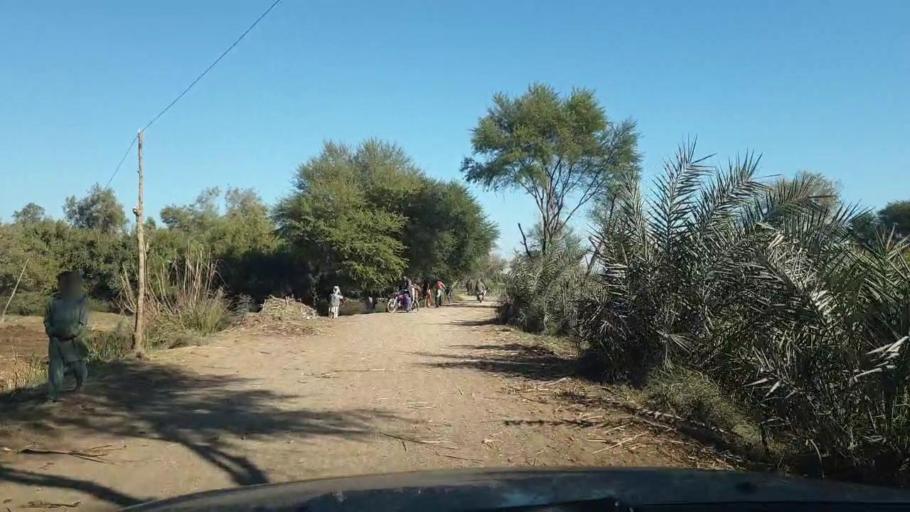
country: PK
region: Sindh
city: Ghotki
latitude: 28.0184
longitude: 69.2826
